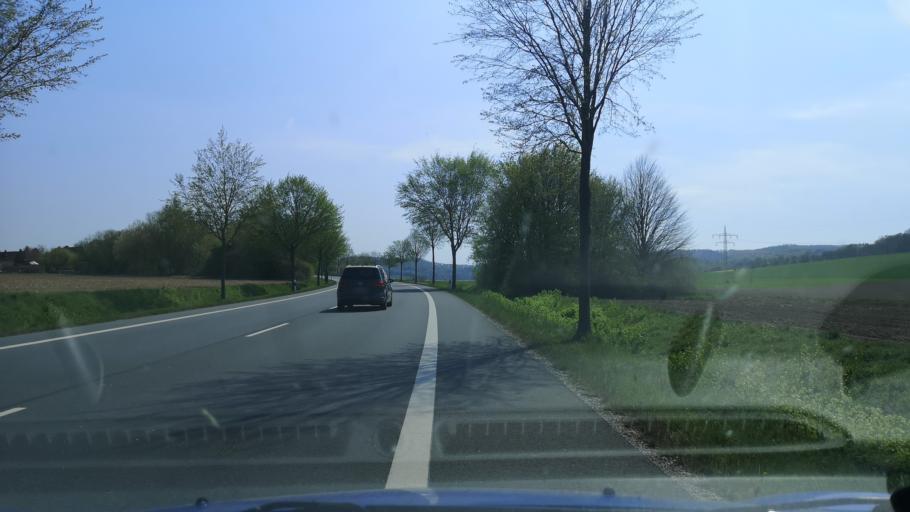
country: DE
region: Lower Saxony
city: Dielmissen
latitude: 51.9642
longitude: 9.6006
